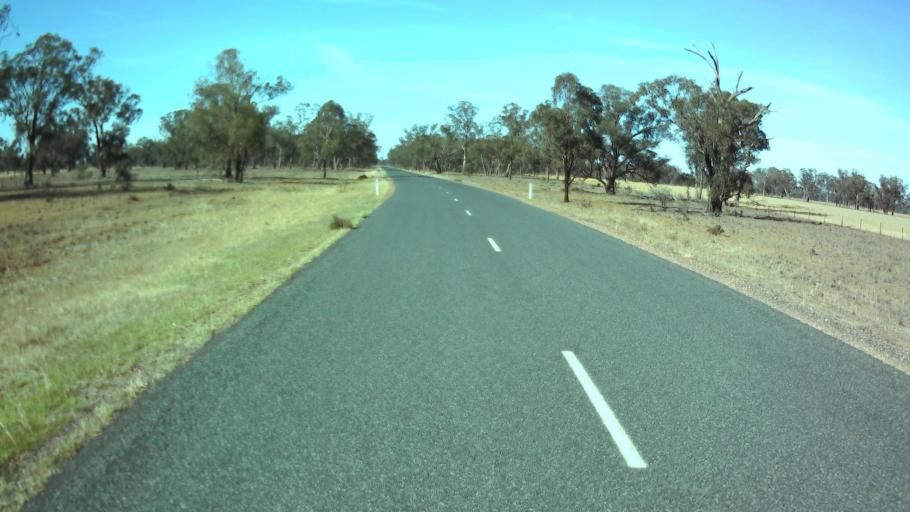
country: AU
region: New South Wales
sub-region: Weddin
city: Grenfell
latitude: -34.0595
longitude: 147.9107
